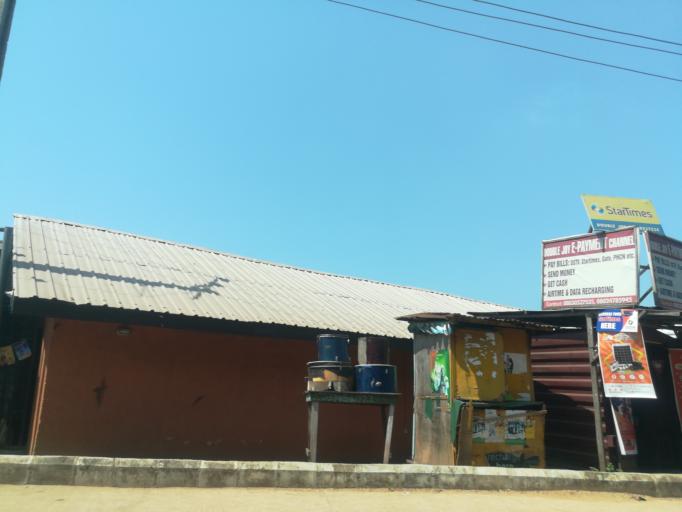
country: NG
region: Ogun
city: Abeokuta
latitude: 7.1481
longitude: 3.3620
